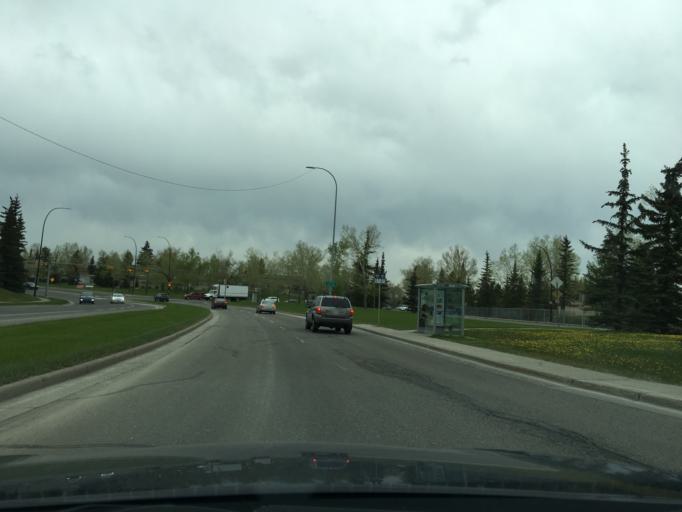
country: CA
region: Alberta
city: Calgary
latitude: 50.9524
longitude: -114.0602
